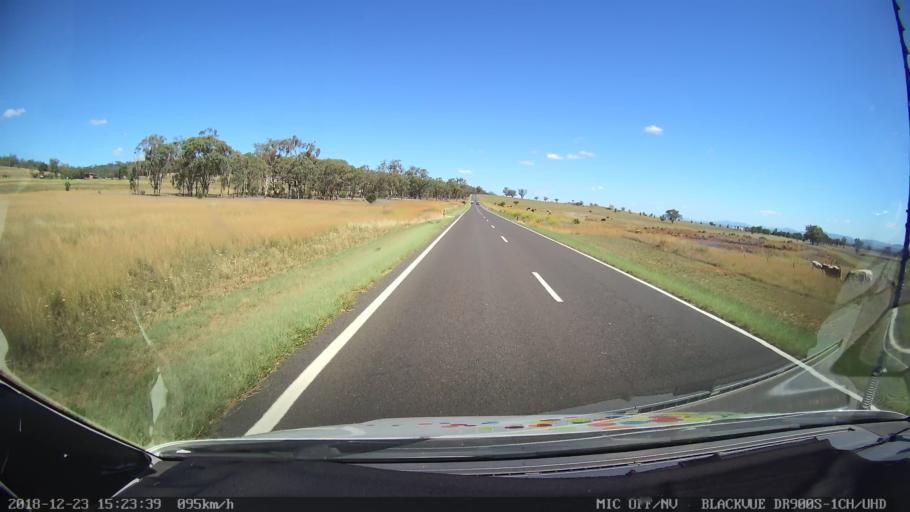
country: AU
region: New South Wales
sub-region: Tamworth Municipality
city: Manilla
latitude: -30.8827
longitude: 150.8162
